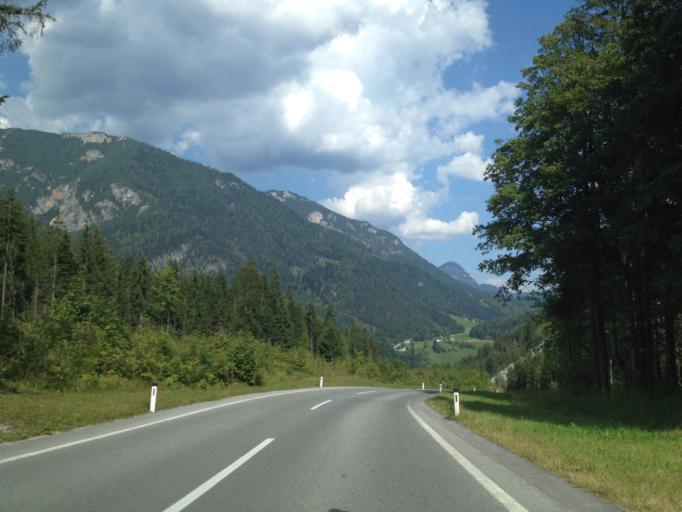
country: AT
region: Styria
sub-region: Politischer Bezirk Liezen
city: Schladming
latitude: 47.4247
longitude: 13.7025
